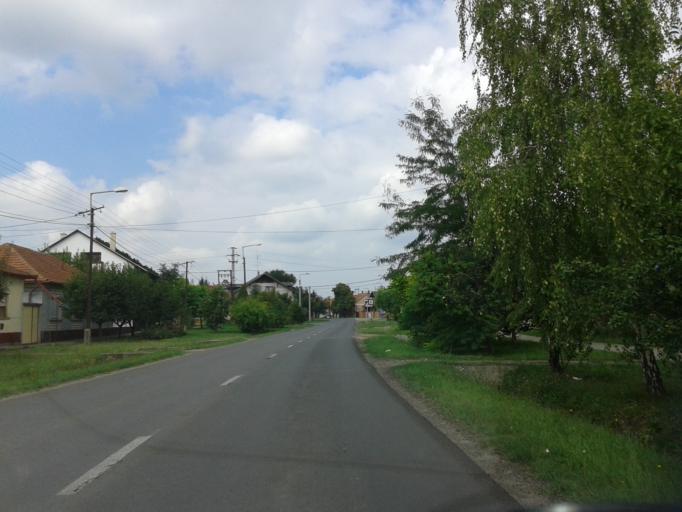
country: HU
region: Csongrad
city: Domaszek
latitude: 46.2763
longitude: 20.0575
